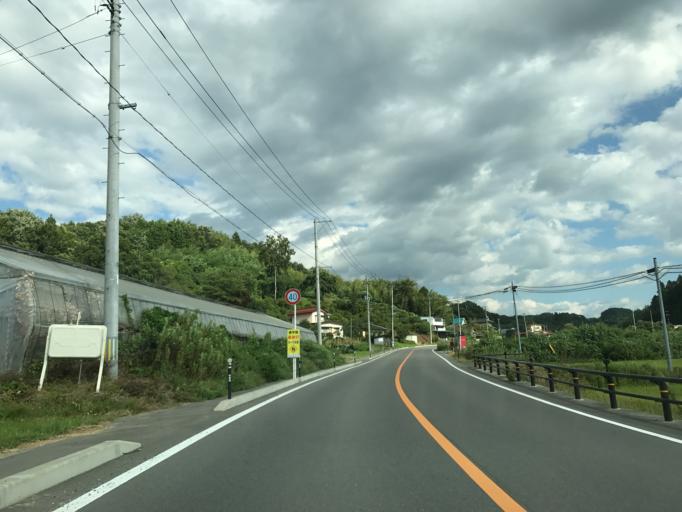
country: JP
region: Fukushima
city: Koriyama
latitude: 37.4094
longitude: 140.4308
